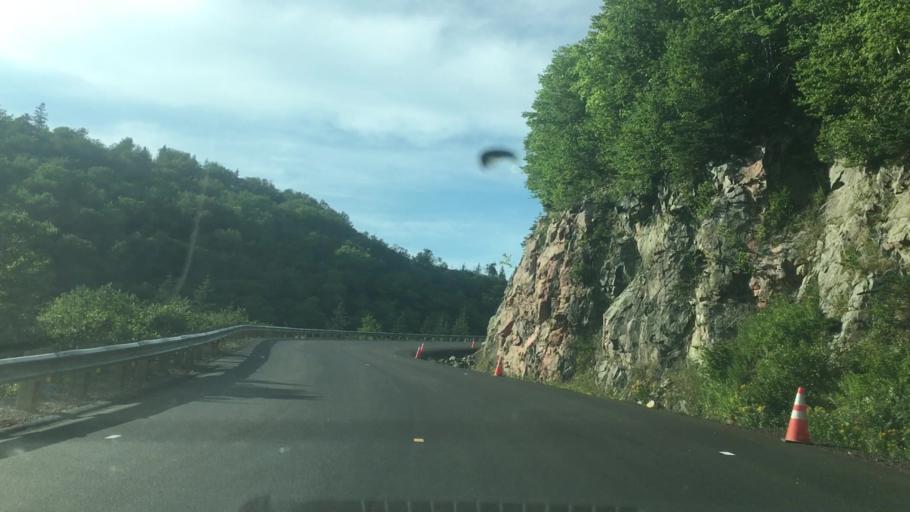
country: CA
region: Nova Scotia
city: Sydney Mines
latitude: 46.8182
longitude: -60.6518
